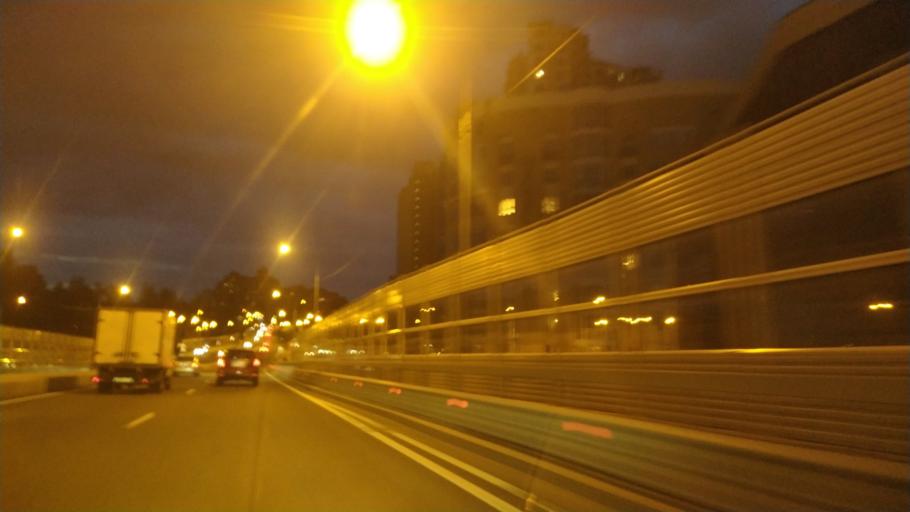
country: RU
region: Leningrad
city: Udel'naya
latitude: 60.0266
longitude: 30.3122
